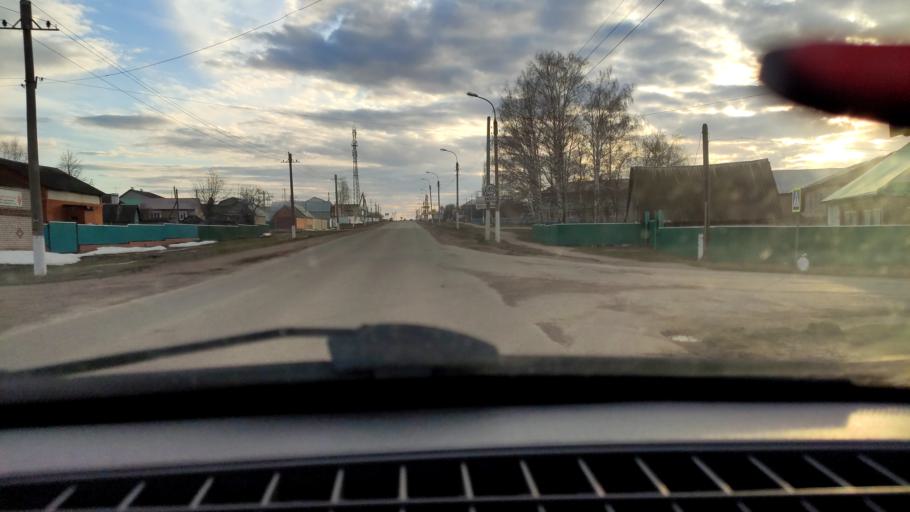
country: RU
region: Bashkortostan
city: Tolbazy
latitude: 54.0102
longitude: 55.8845
